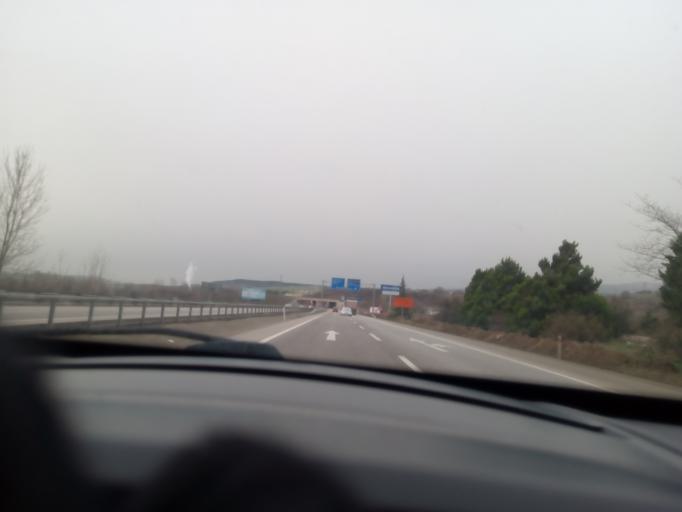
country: TR
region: Balikesir
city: Gobel
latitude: 39.9757
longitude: 28.1781
